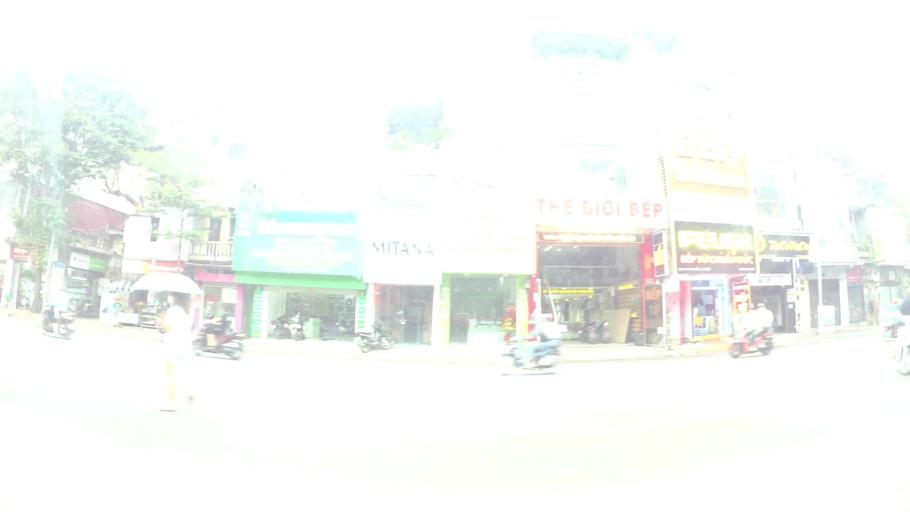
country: VN
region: Ha Noi
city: Dong Da
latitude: 21.0113
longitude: 105.8254
